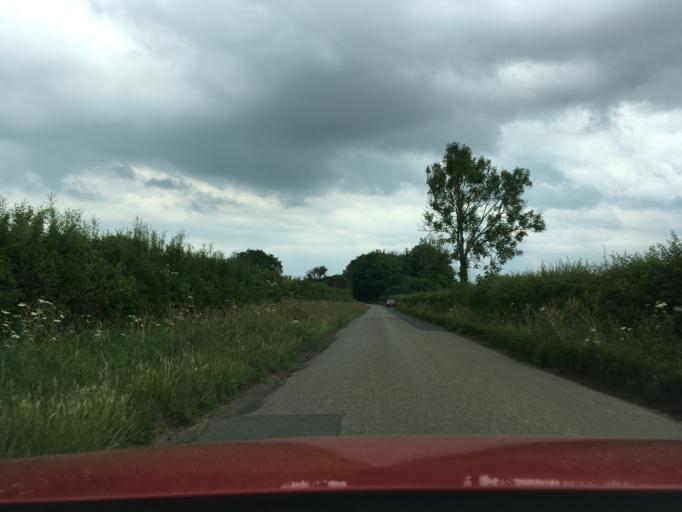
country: GB
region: England
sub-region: Gloucestershire
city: Coates
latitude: 51.7455
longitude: -2.0550
